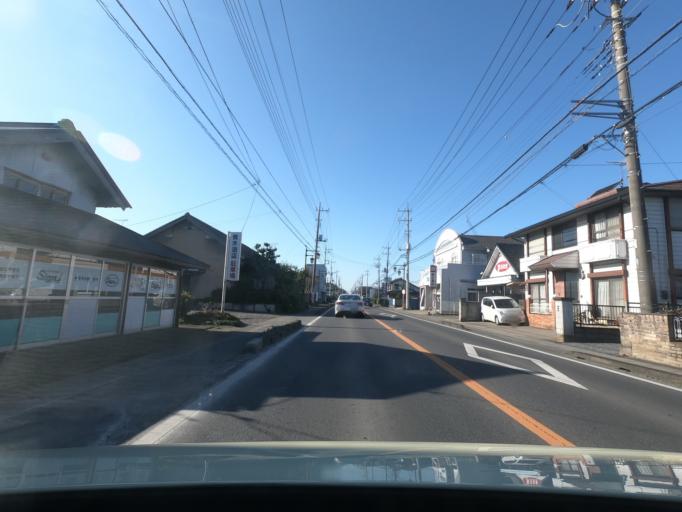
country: JP
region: Ibaraki
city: Ishige
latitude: 36.1844
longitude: 139.9480
